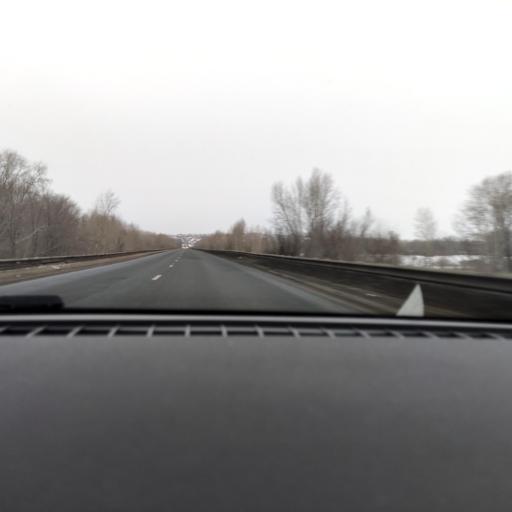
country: RU
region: Samara
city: Smyshlyayevka
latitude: 53.2183
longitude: 50.5019
